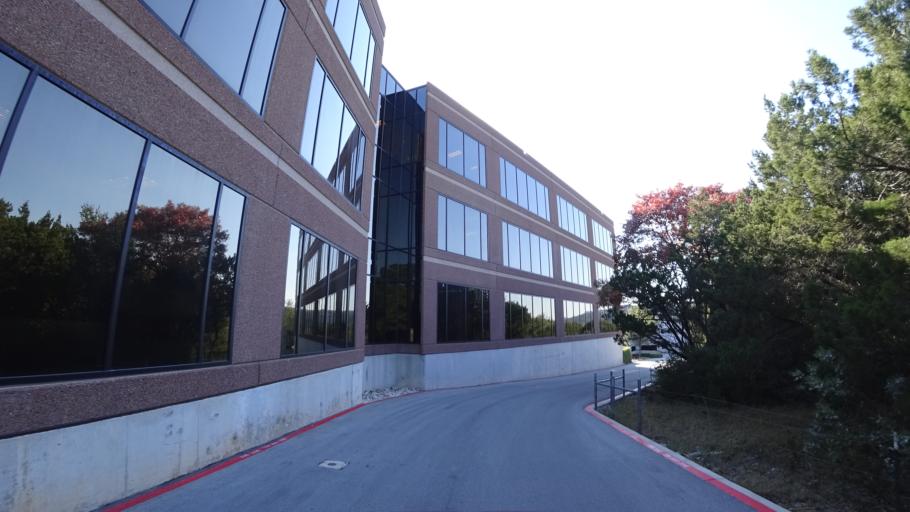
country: US
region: Texas
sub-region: Williamson County
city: Jollyville
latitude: 30.3876
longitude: -97.7691
